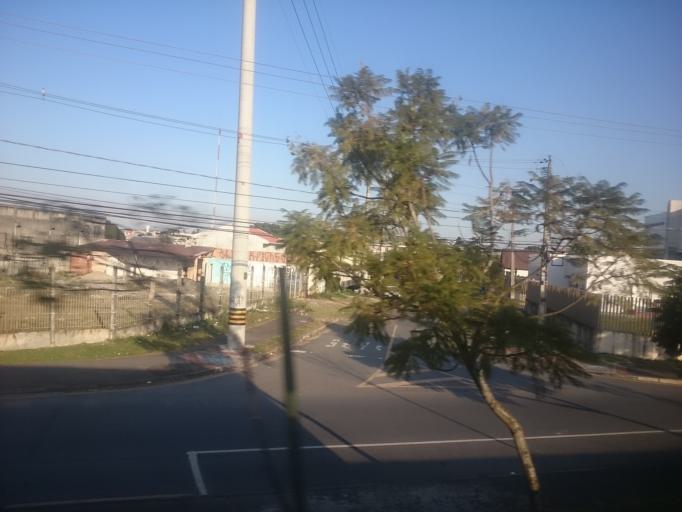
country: BR
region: Parana
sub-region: Curitiba
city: Curitiba
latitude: -25.4906
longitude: -49.2710
